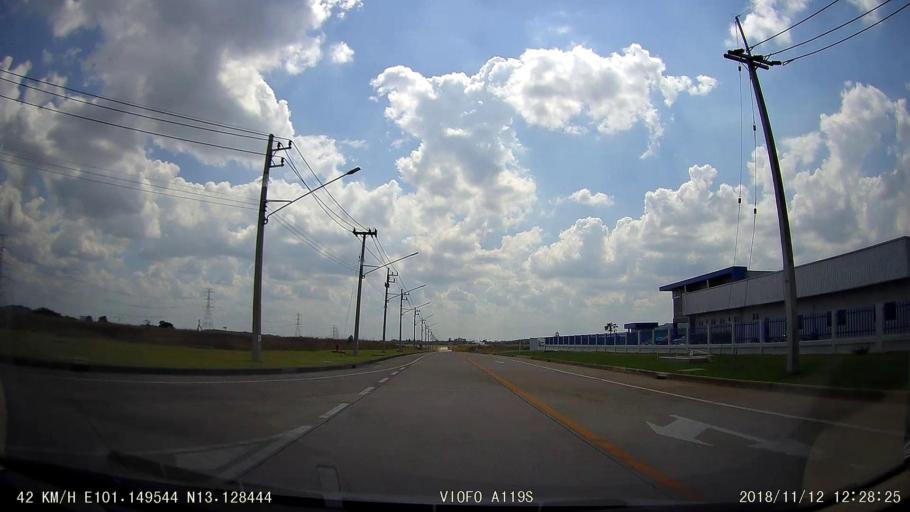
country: TH
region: Chon Buri
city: Ban Talat Bueng
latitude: 13.1280
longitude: 101.1495
